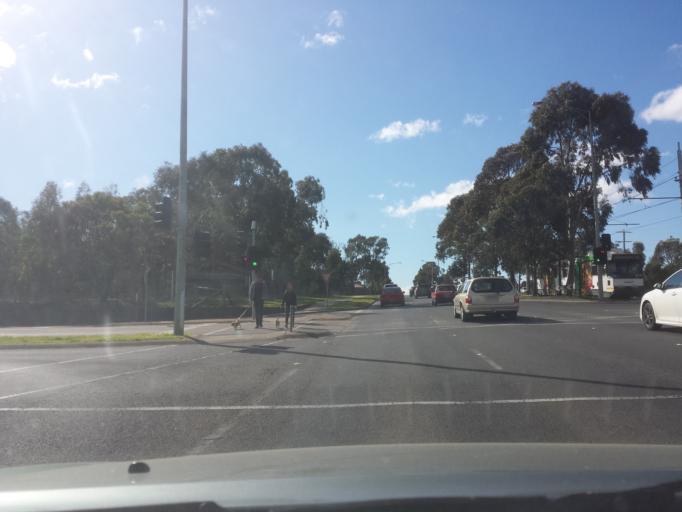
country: AU
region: Victoria
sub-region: Banyule
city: Bundoora
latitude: -37.7091
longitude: 145.0503
